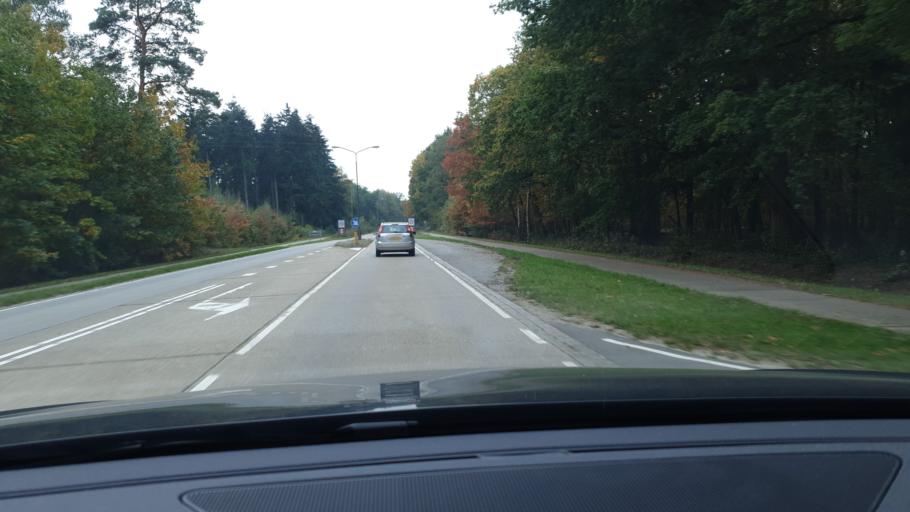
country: NL
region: North Brabant
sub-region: Gemeente Veldhoven
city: Oerle
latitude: 51.3861
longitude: 5.3769
